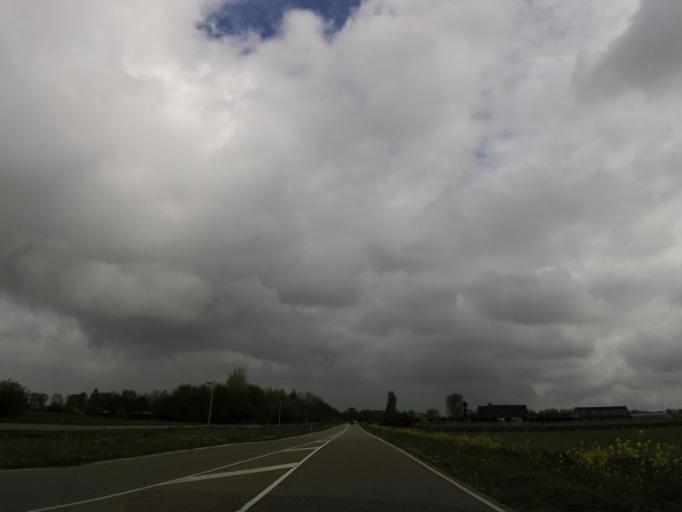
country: NL
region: Gelderland
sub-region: Gemeente Culemborg
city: Culemborg
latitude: 51.9375
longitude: 5.1864
